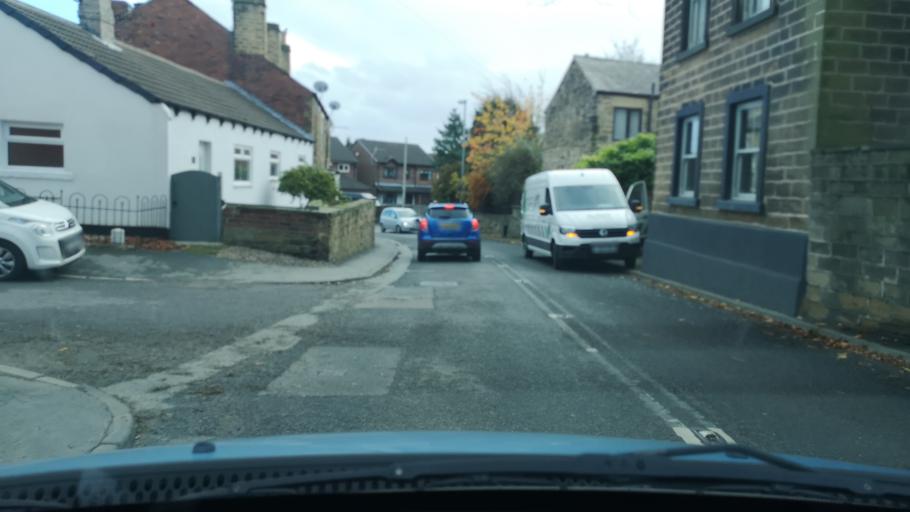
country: GB
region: England
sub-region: City and Borough of Wakefield
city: Ryhill
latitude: 53.6093
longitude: -1.4023
